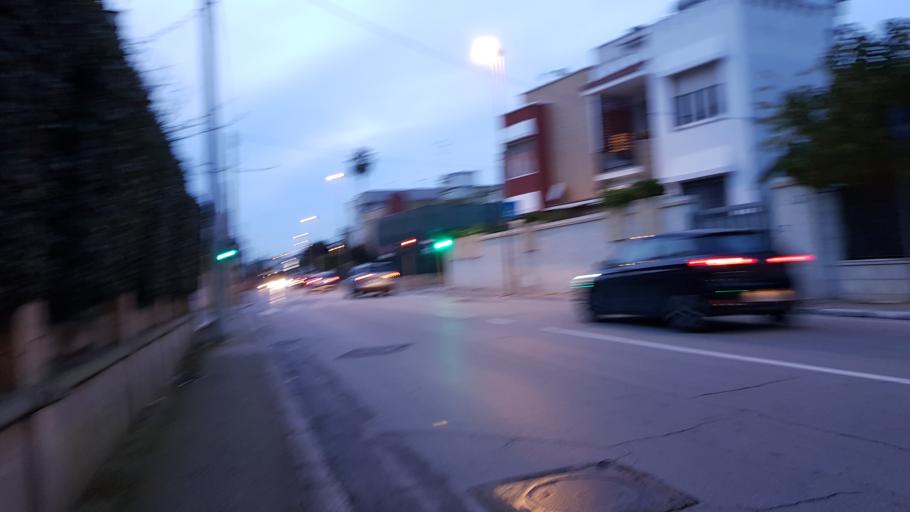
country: IT
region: Apulia
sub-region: Provincia di Brindisi
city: Materdomini
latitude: 40.6485
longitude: 17.9436
